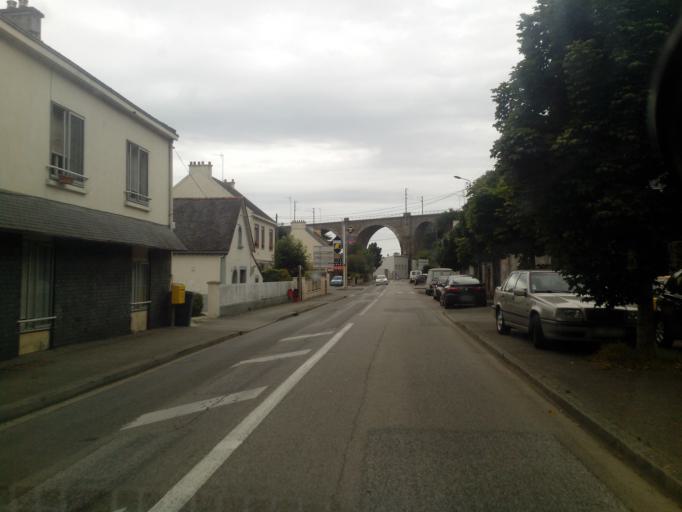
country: FR
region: Brittany
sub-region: Departement du Morbihan
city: Hennebont
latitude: 47.7966
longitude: -3.2750
